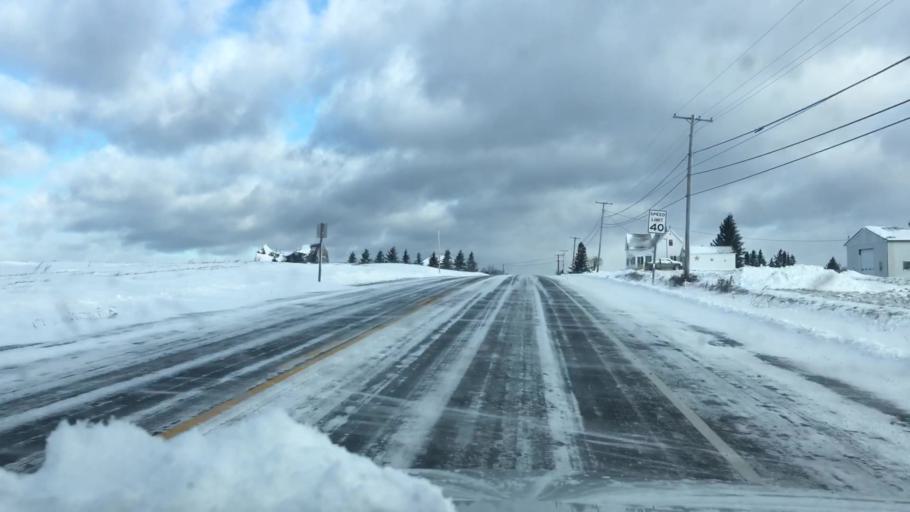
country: US
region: Maine
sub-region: Aroostook County
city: Caribou
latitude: 46.9361
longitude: -68.0232
